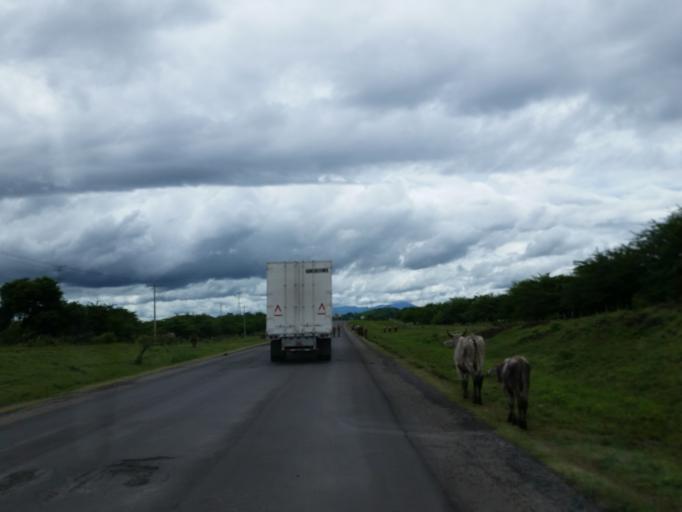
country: NI
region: Chinandega
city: Somotillo
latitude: 12.8919
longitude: -86.8505
